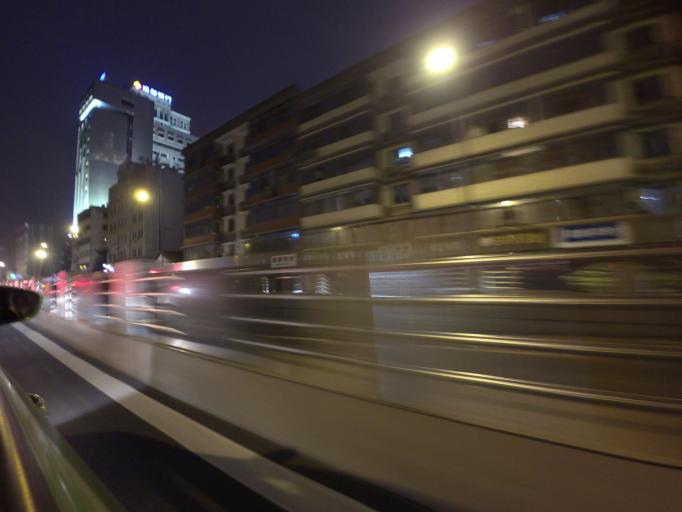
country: CN
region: Sichuan
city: Chengdu
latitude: 30.6574
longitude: 104.0583
